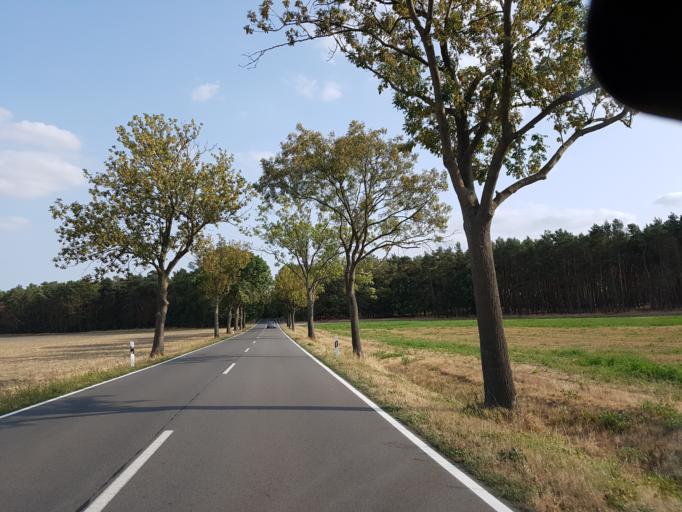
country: DE
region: Saxony-Anhalt
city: Pretzsch
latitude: 51.7391
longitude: 12.7600
